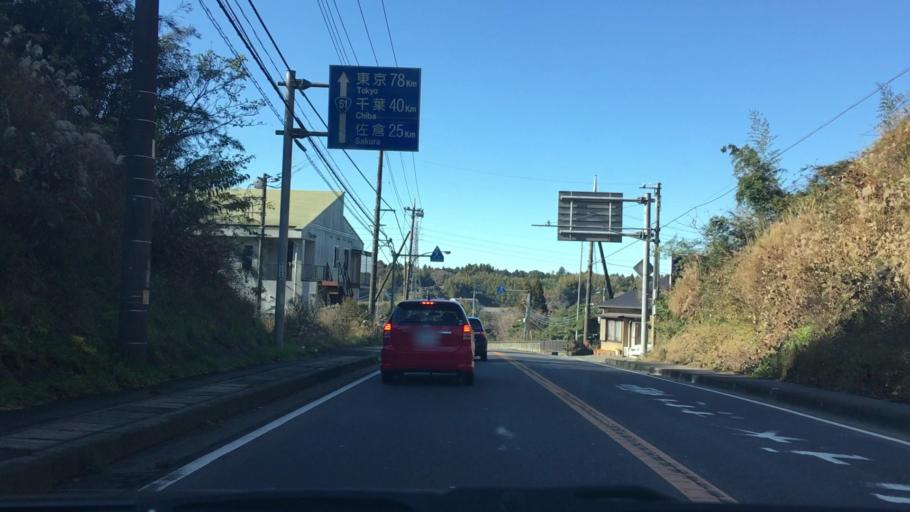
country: JP
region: Chiba
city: Sawara
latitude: 35.8344
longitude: 140.4266
